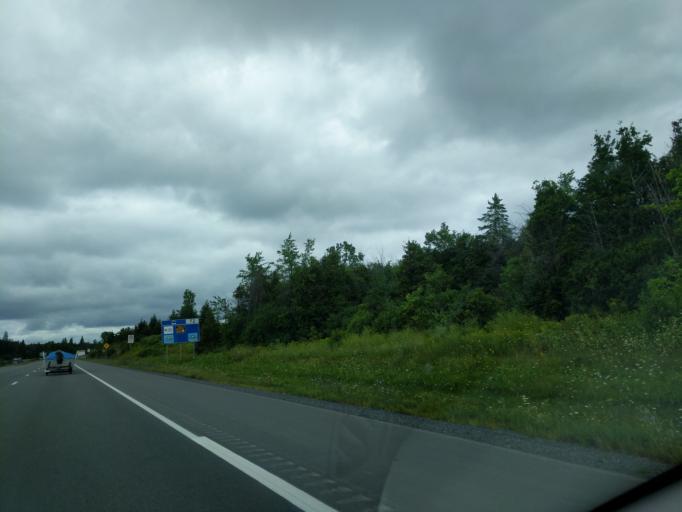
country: CA
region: Ontario
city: Bells Corners
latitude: 45.2783
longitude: -75.8021
